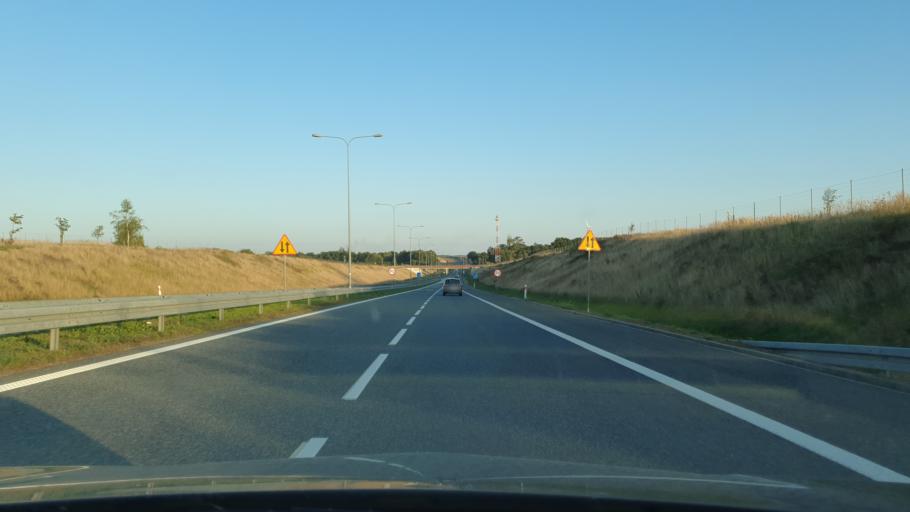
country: PL
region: Pomeranian Voivodeship
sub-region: Powiat slupski
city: Kobylnica
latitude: 54.4353
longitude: 16.9627
